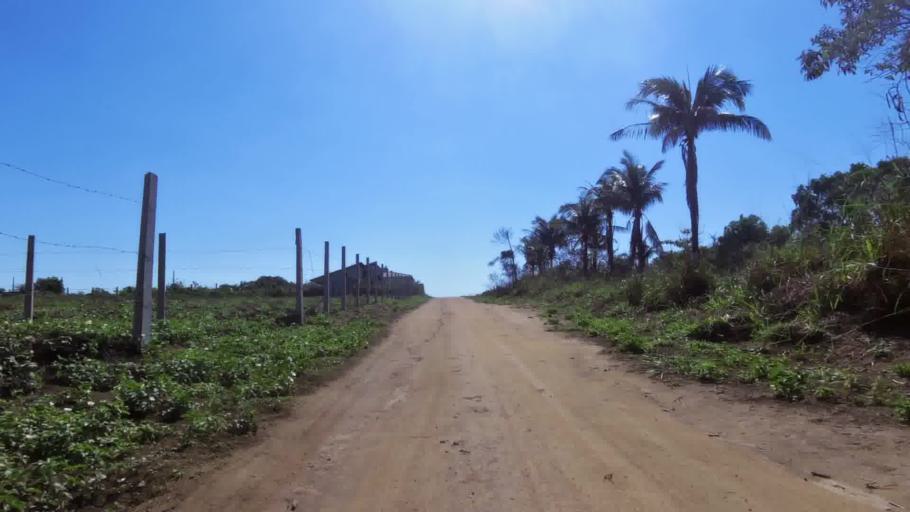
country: BR
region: Espirito Santo
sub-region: Guarapari
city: Guarapari
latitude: -20.7358
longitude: -40.5503
